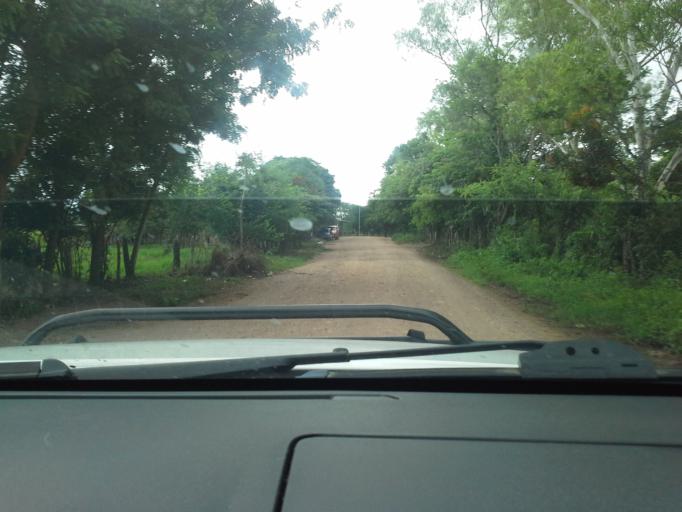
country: NI
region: Matagalpa
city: Ciudad Dario
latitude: 12.8339
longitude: -86.2112
